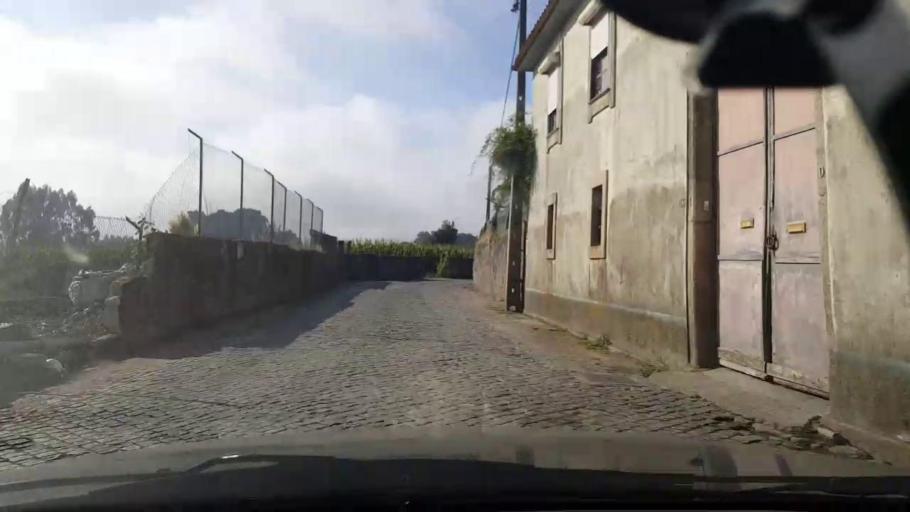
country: PT
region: Porto
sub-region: Maia
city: Gemunde
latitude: 41.2671
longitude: -8.6736
